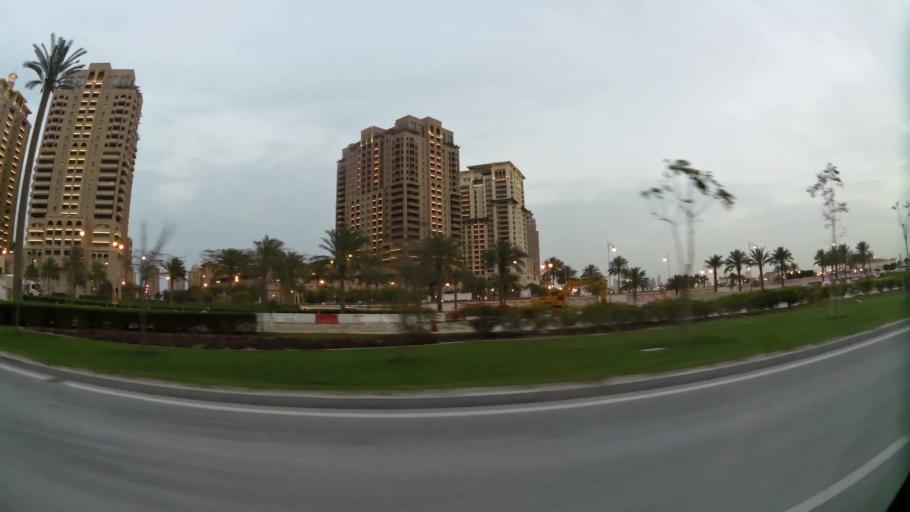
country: QA
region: Baladiyat ad Dawhah
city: Doha
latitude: 25.3732
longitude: 51.5385
